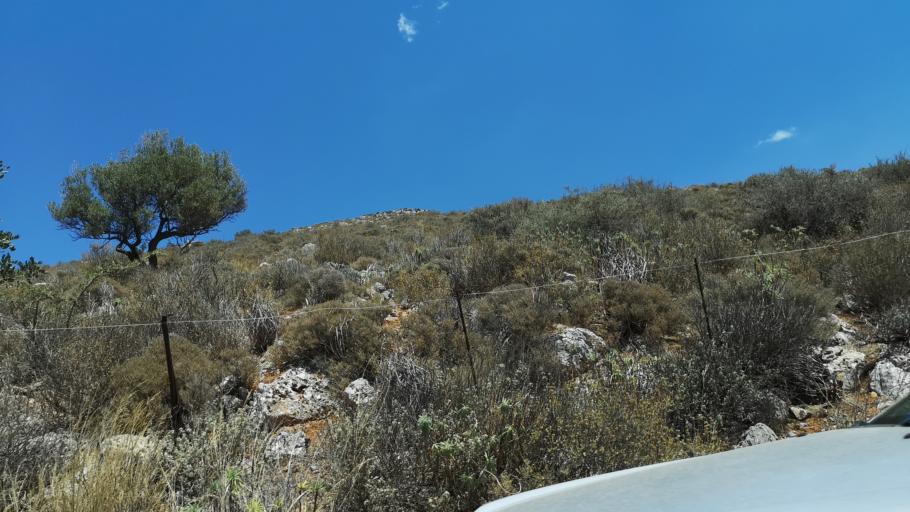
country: GR
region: Crete
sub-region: Nomos Lasithiou
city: Neapoli
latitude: 35.2515
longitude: 25.6330
